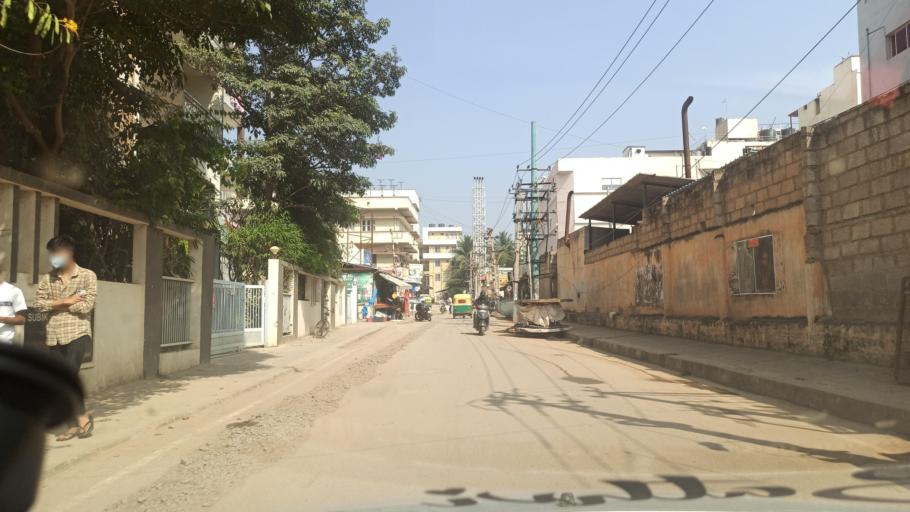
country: IN
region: Karnataka
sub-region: Bangalore Urban
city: Bangalore
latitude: 12.9519
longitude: 77.6980
